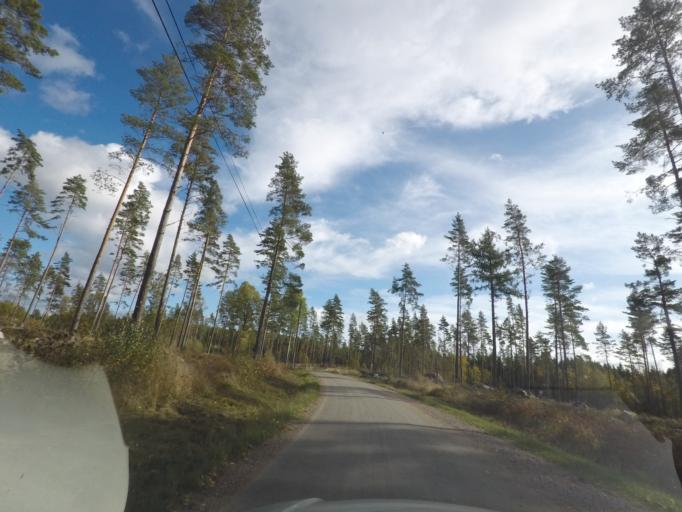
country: SE
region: Vaestmanland
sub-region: Kungsors Kommun
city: Kungsoer
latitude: 59.3378
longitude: 16.2090
